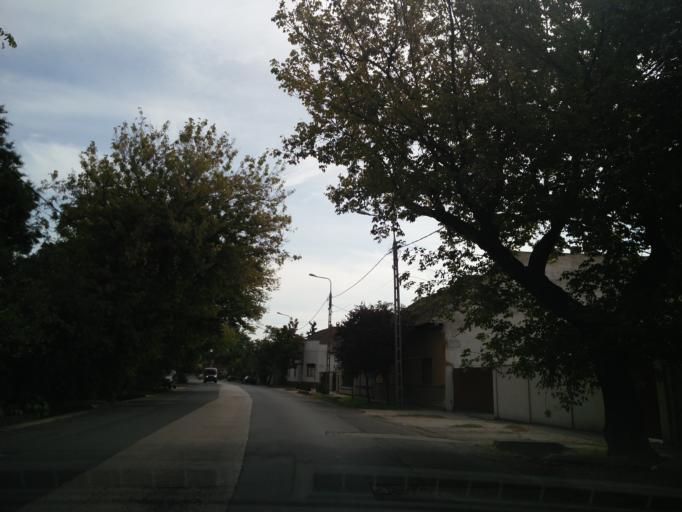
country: HU
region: Budapest
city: Budapest XV. keruelet
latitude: 47.5651
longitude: 19.1246
